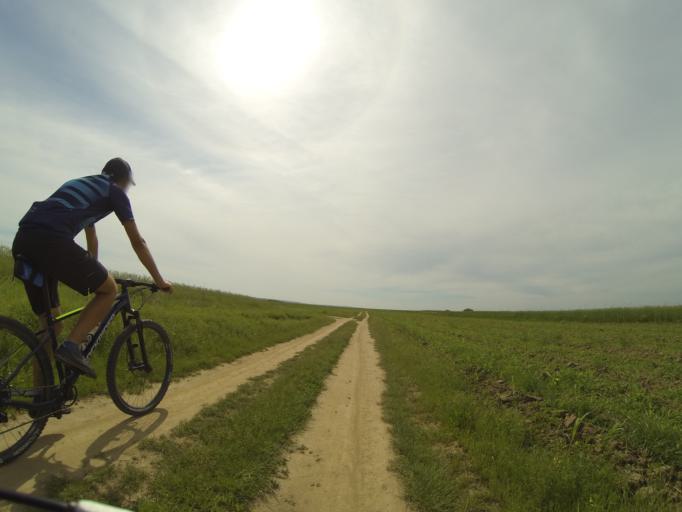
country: RO
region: Dolj
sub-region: Comuna Malu Mare
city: Preajba
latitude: 44.2603
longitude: 23.8622
